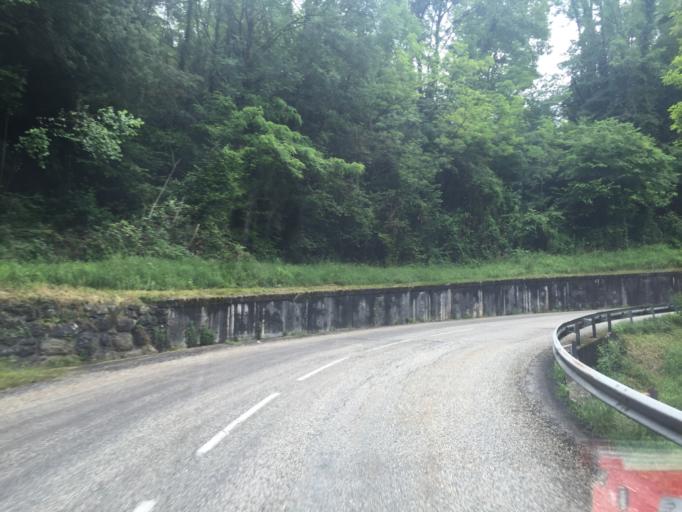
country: FR
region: Rhone-Alpes
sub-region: Departement de la Savoie
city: Barby
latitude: 45.5894
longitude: 6.0222
